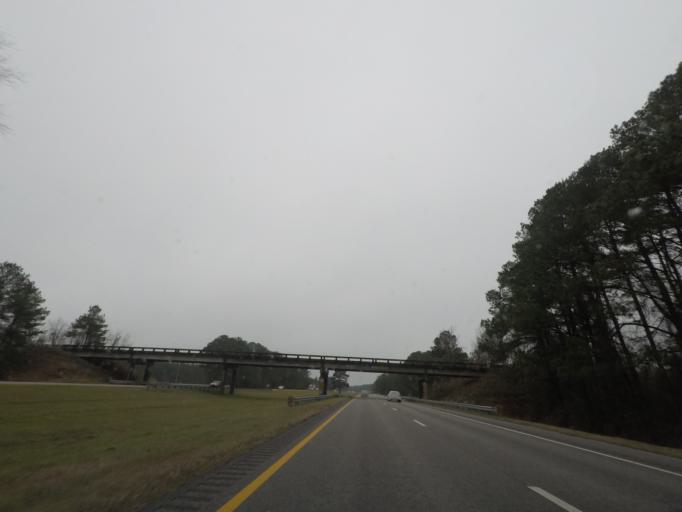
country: US
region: South Carolina
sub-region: Florence County
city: Timmonsville
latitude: 33.9865
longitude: -80.0251
